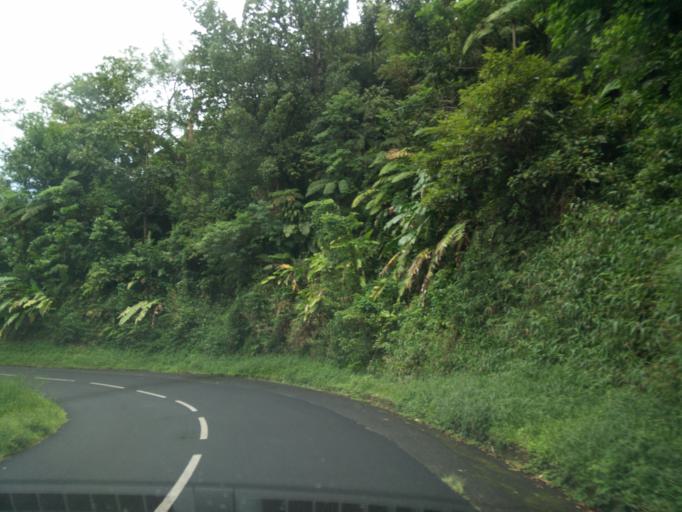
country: MQ
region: Martinique
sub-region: Martinique
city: Le Morne-Rouge
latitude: 14.7269
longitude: -61.1113
